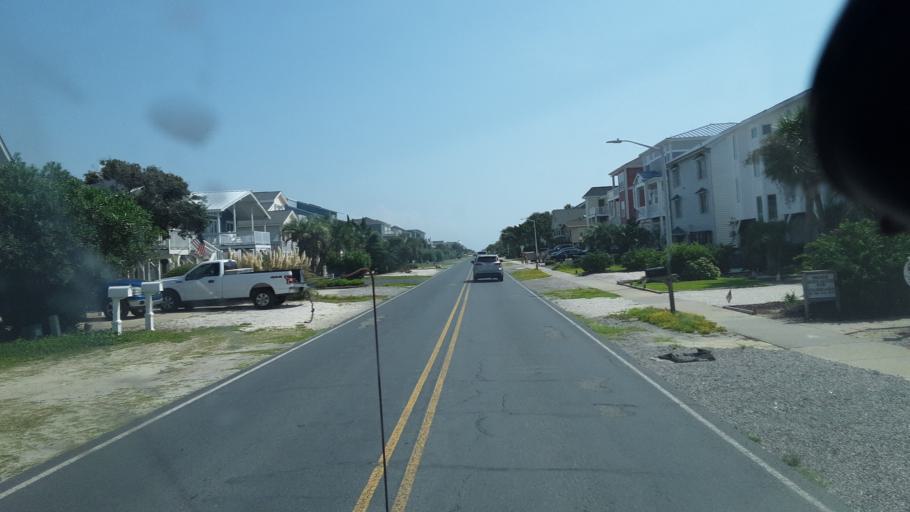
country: US
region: North Carolina
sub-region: Brunswick County
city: Sunset Beach
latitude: 33.8831
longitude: -78.4538
